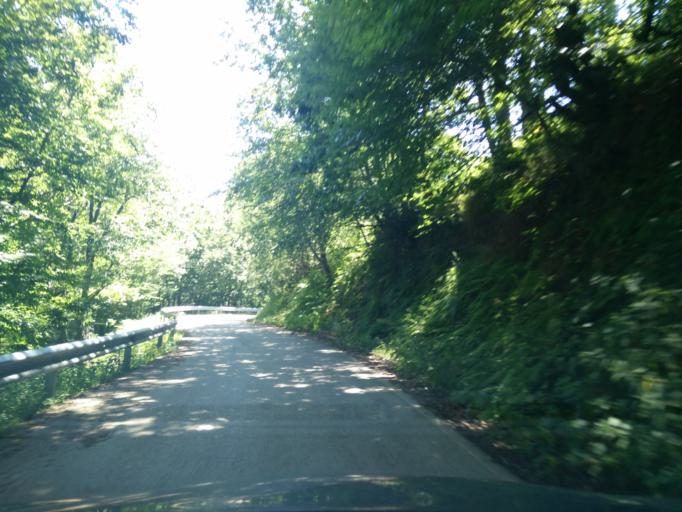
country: ES
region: Asturias
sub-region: Province of Asturias
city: Amieva
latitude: 43.1943
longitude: -5.1352
